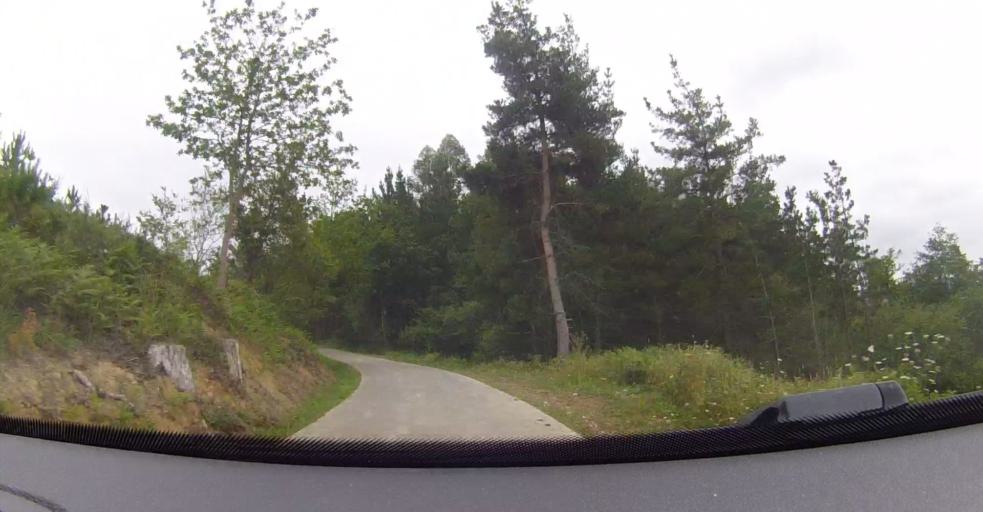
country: ES
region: Basque Country
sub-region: Bizkaia
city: Urrestieta
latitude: 43.2292
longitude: -3.1727
